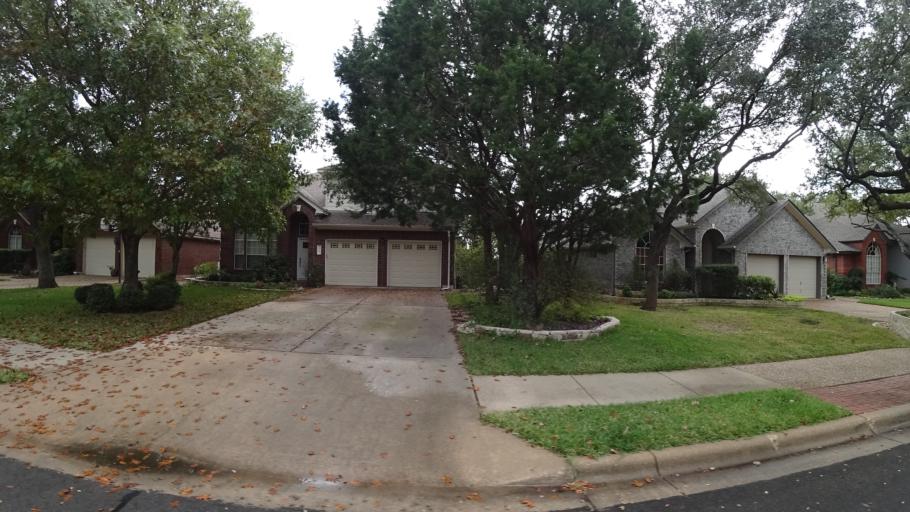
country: US
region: Texas
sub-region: Williamson County
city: Brushy Creek
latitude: 30.5159
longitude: -97.7149
